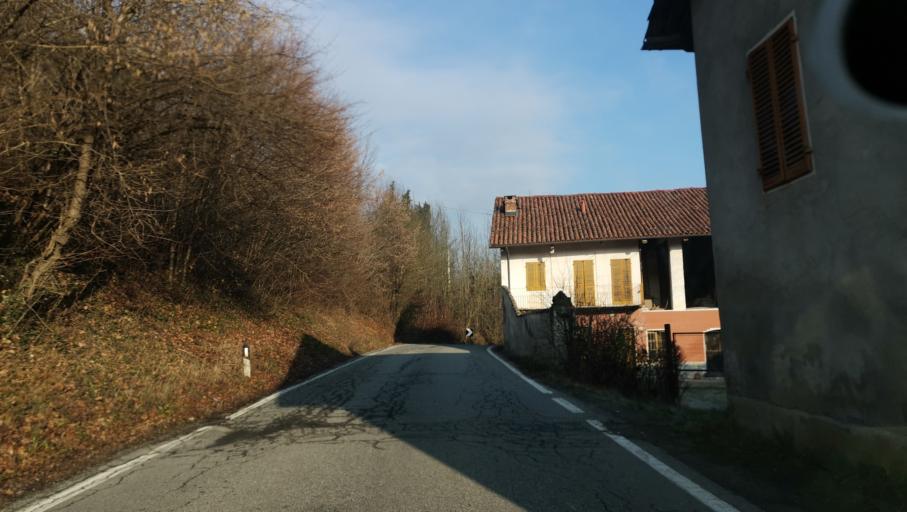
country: IT
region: Piedmont
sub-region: Provincia di Torino
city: Casalborgone
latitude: 45.1117
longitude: 7.9418
